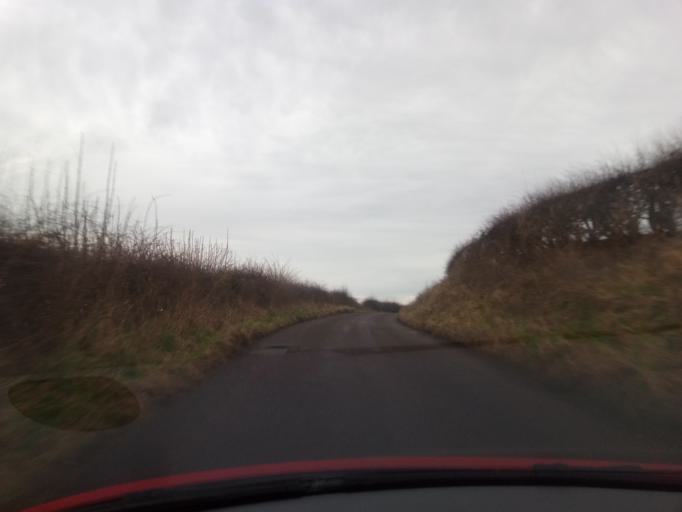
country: GB
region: England
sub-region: Northumberland
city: Wooler
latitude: 55.5524
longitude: -2.0335
